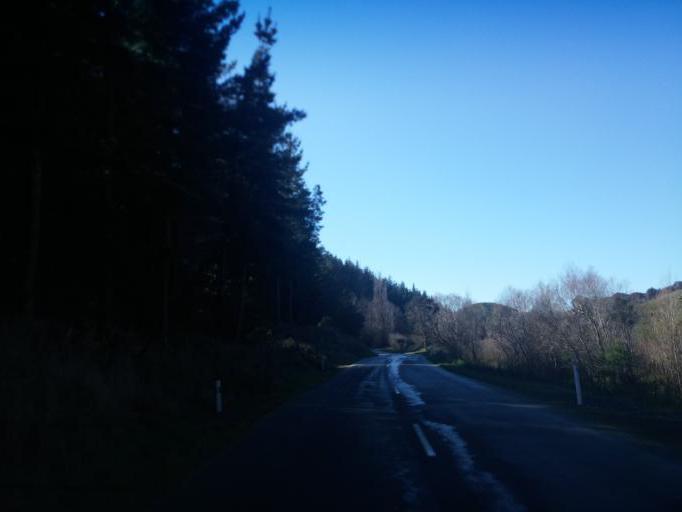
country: NZ
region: Wellington
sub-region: South Wairarapa District
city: Waipawa
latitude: -41.3832
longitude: 175.4992
